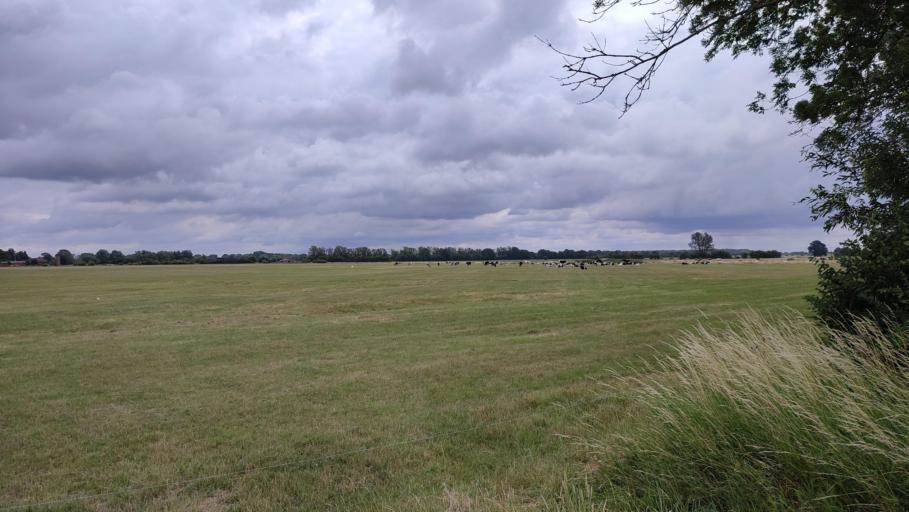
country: DE
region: Lower Saxony
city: Hitzacker
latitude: 53.1738
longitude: 11.1014
